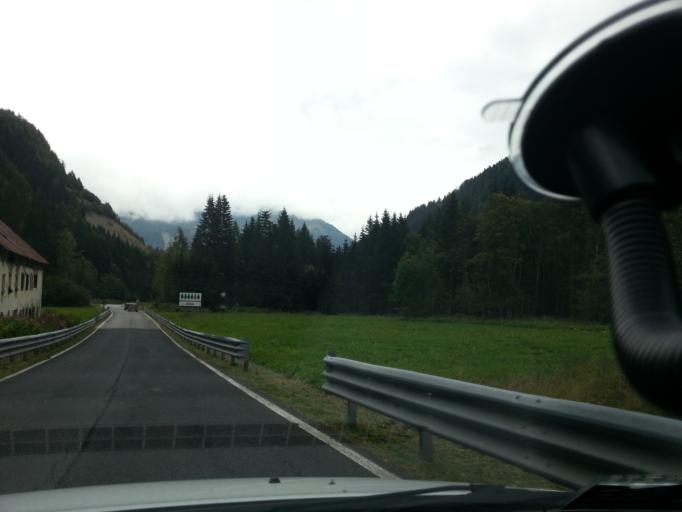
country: IT
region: Friuli Venezia Giulia
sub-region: Provincia di Udine
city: Forni Avoltri
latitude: 46.5709
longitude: 12.7420
